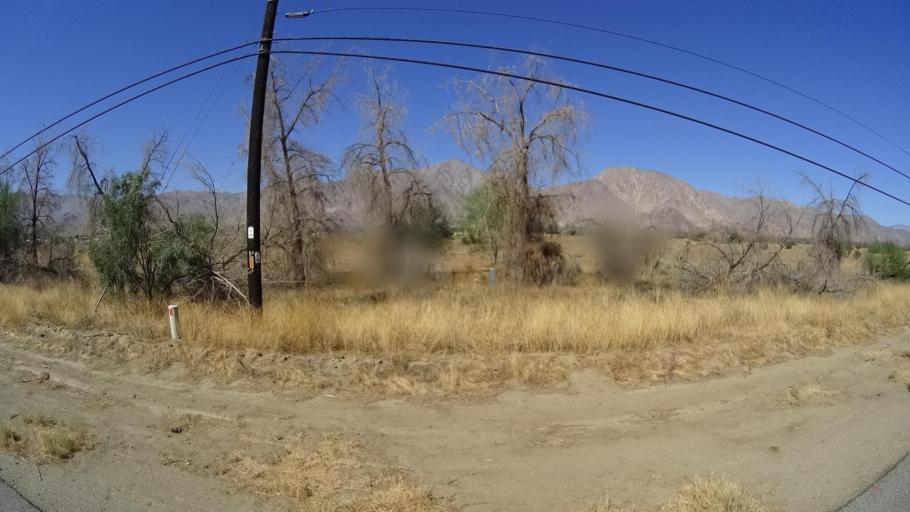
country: US
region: California
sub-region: San Diego County
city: Borrego Springs
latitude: 33.2695
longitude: -116.3662
